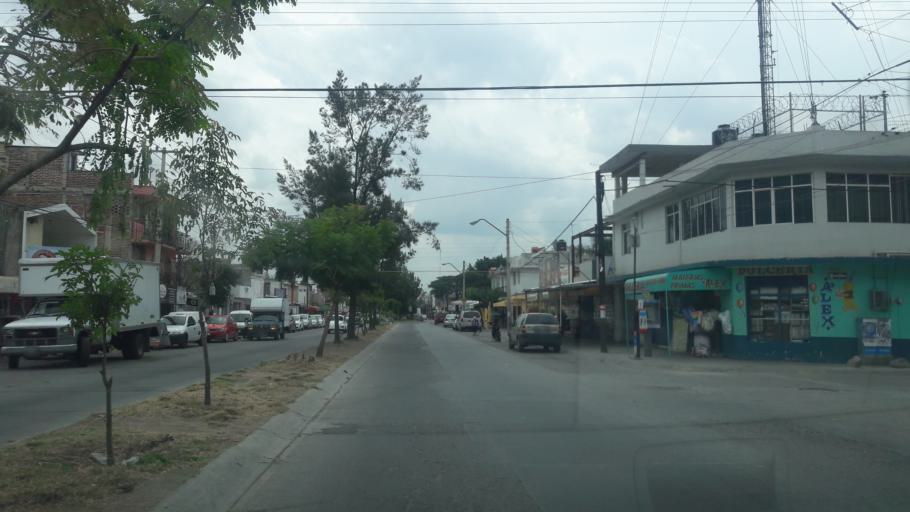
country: MX
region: Guanajuato
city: Leon
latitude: 21.1817
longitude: -101.6670
